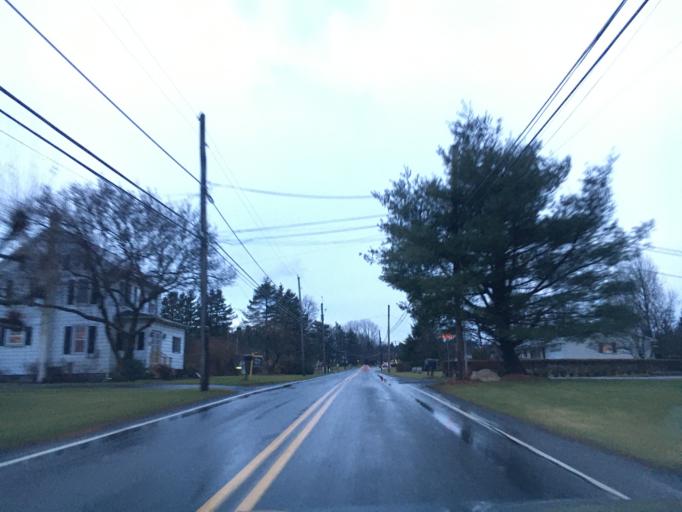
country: US
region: Pennsylvania
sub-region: Northampton County
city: Bath
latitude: 40.7713
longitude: -75.4212
